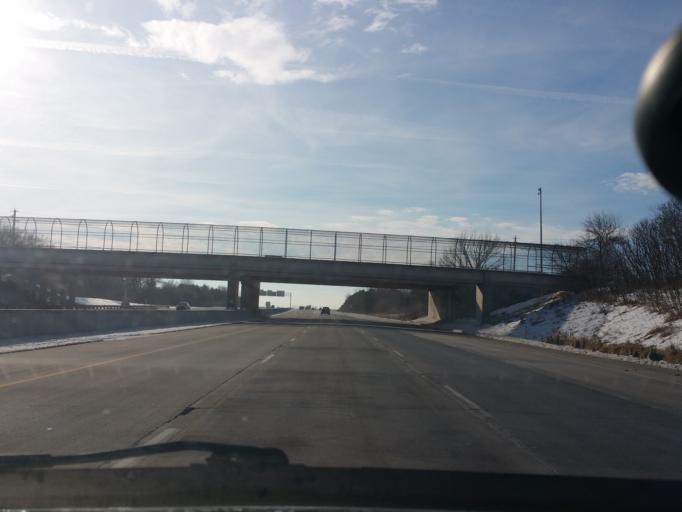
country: US
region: Iowa
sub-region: Polk County
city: Clive
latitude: 41.5858
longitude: -93.7778
